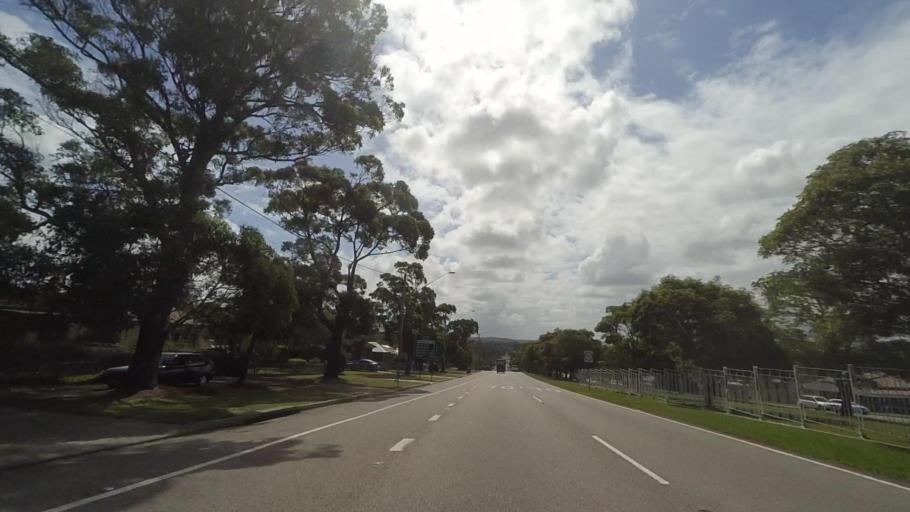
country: AU
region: New South Wales
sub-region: Newcastle
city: North Lambton
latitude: -32.9089
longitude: 151.7011
